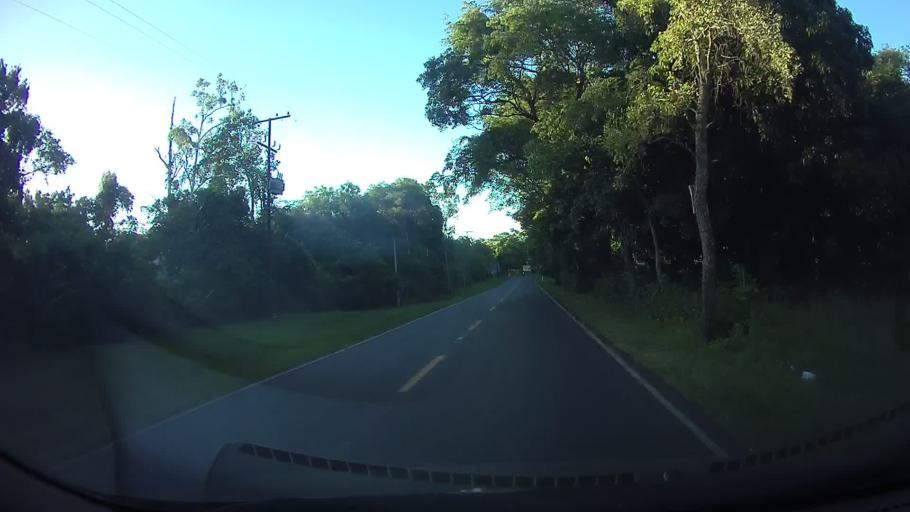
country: PY
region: Central
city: Aregua
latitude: -25.2706
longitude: -57.4116
